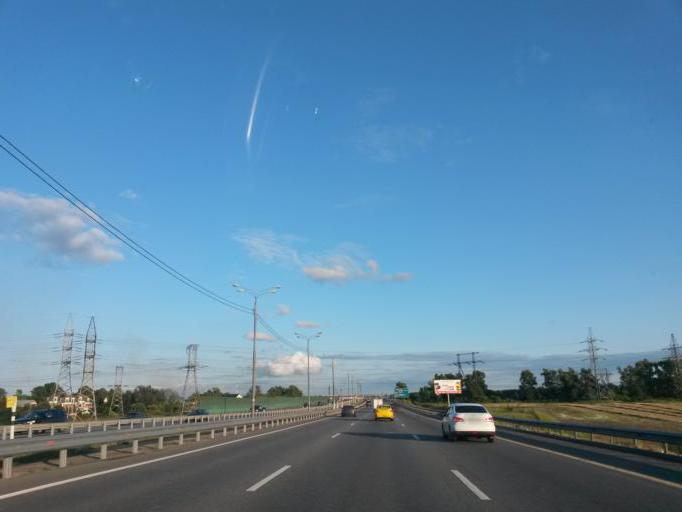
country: RU
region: Moskovskaya
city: Yam
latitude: 55.4912
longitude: 37.7356
